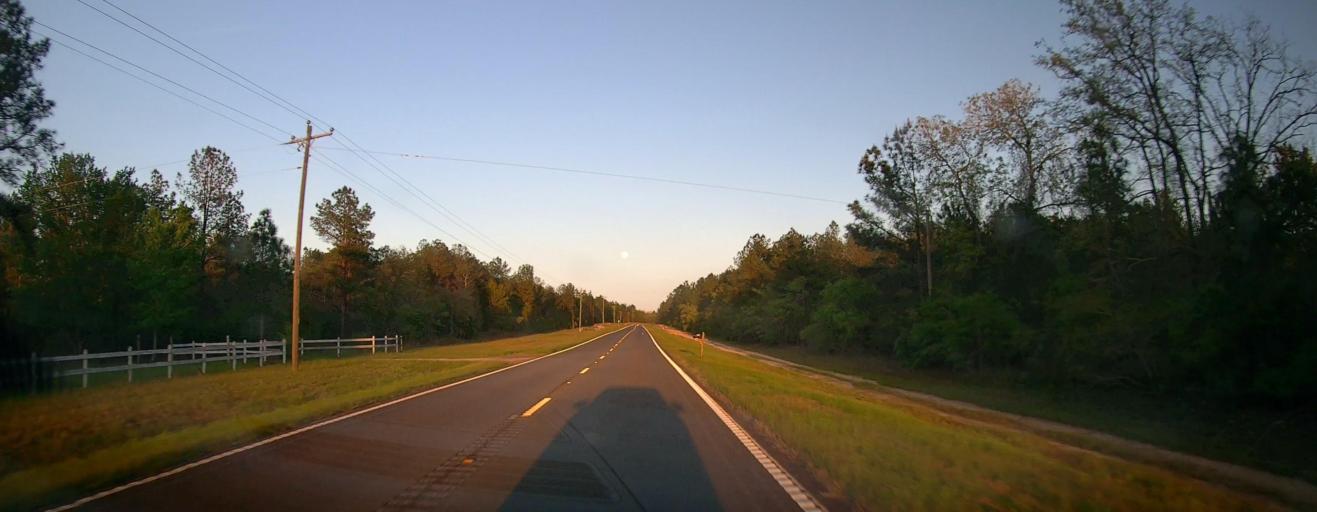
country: US
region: Georgia
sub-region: Marion County
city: Buena Vista
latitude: 32.4424
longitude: -84.6119
